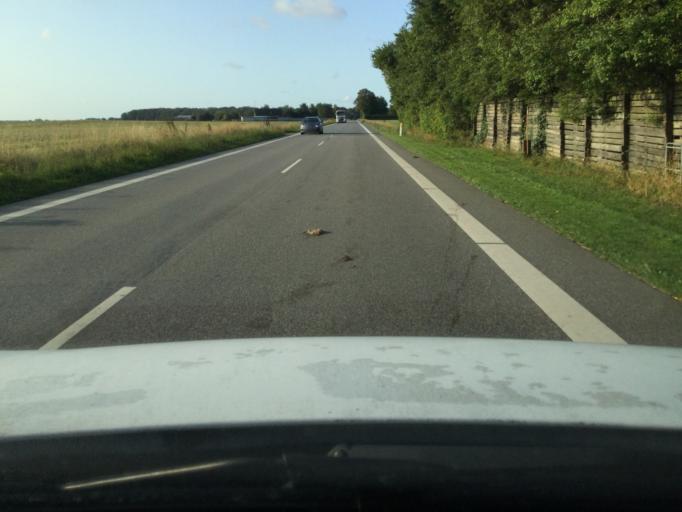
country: DK
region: Zealand
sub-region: Lolland Kommune
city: Rodby
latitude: 54.7409
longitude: 11.3889
